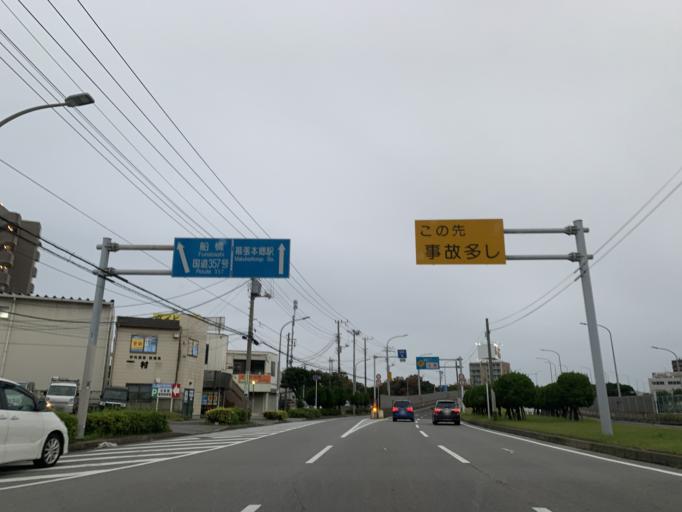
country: JP
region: Chiba
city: Funabashi
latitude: 35.6561
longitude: 140.0332
